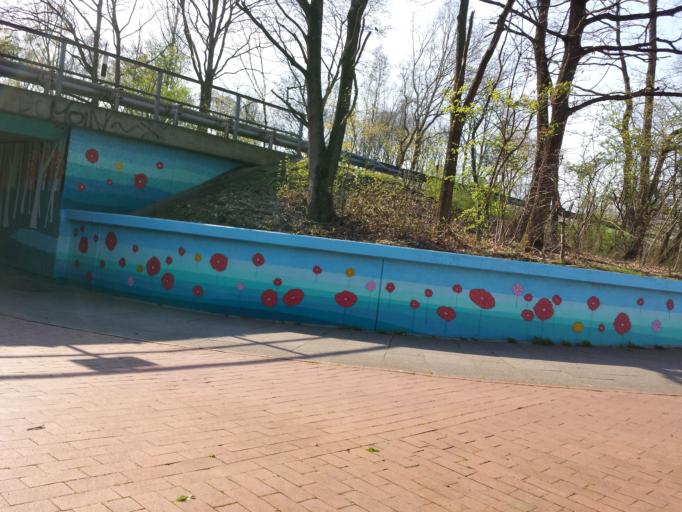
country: DE
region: Lower Saxony
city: Lilienthal
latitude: 53.0831
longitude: 8.9087
